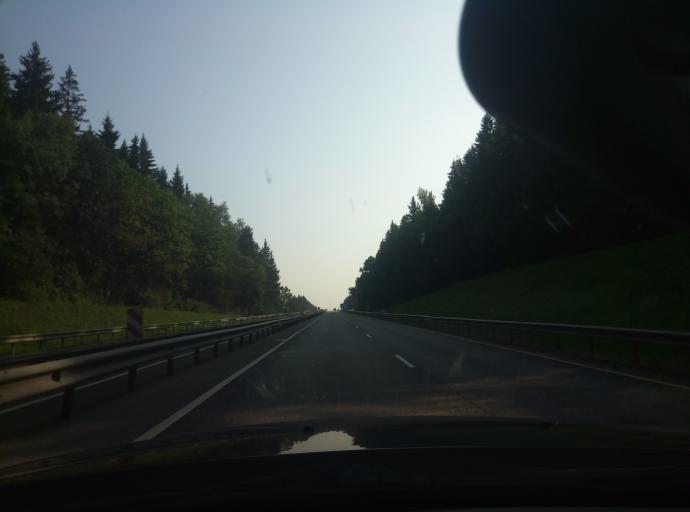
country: RU
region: Kaluga
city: Maloyaroslavets
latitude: 55.0030
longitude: 36.5323
